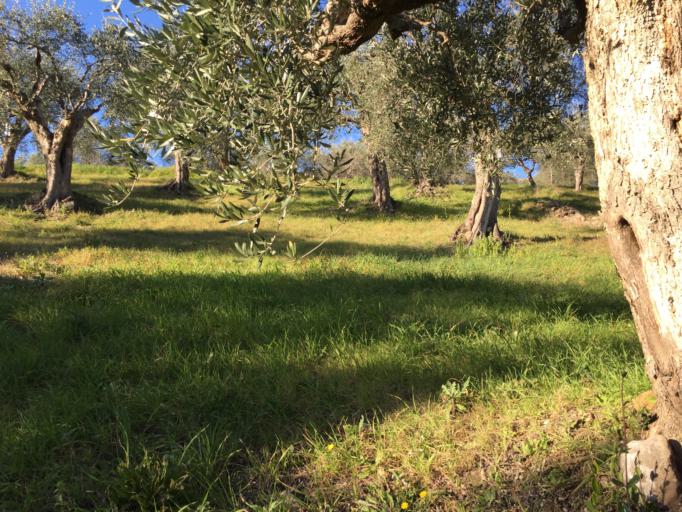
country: IT
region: Campania
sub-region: Provincia di Salerno
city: Salvitelle
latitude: 40.6015
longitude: 15.4806
